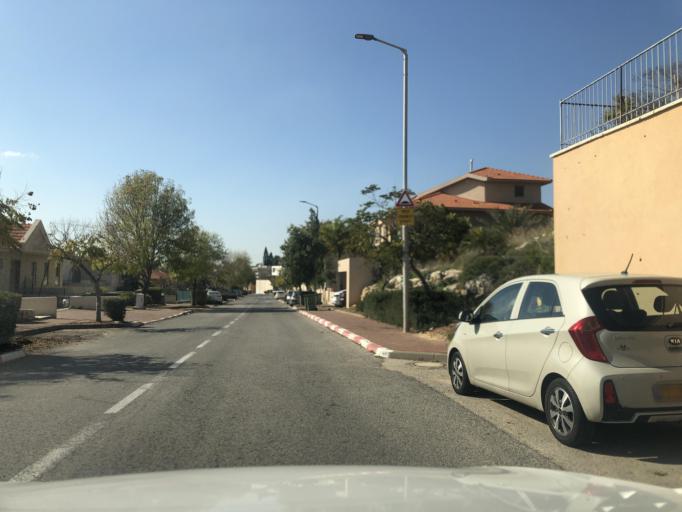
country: PS
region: West Bank
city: Azun Atme
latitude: 32.1137
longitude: 35.0301
